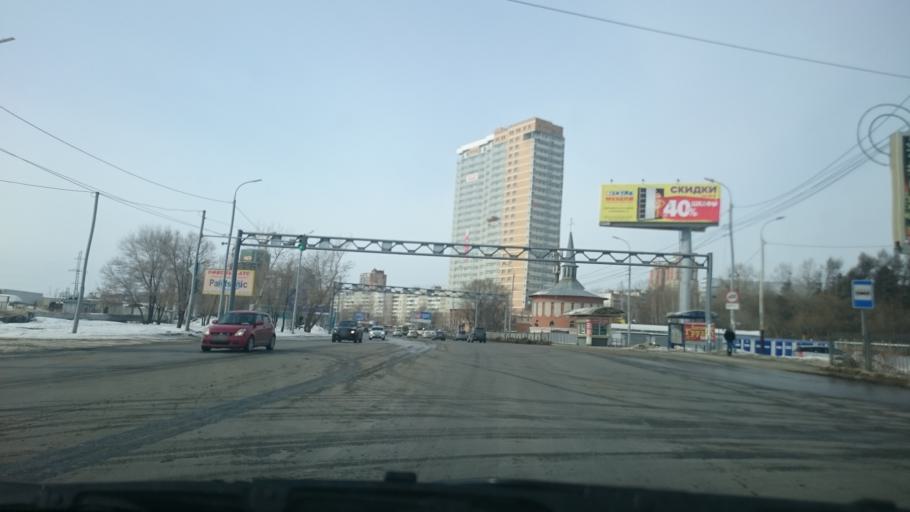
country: RU
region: Khabarovsk Krai
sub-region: Khabarovskiy Rayon
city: Khabarovsk
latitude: 48.4614
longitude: 135.0871
